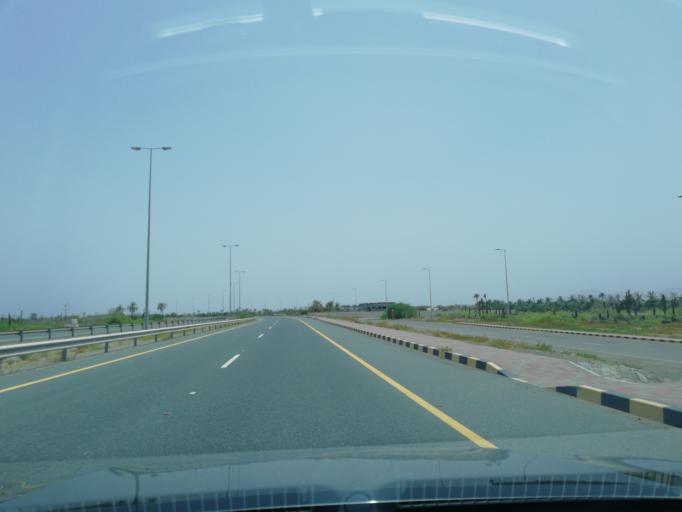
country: OM
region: Al Batinah
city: Shinas
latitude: 24.8400
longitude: 56.4256
